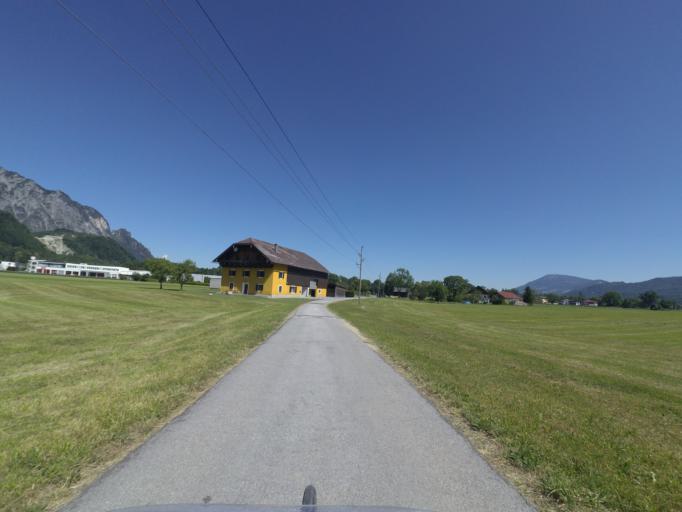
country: AT
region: Salzburg
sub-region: Politischer Bezirk Hallein
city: Puch bei Hallein
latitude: 47.7140
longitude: 13.0672
